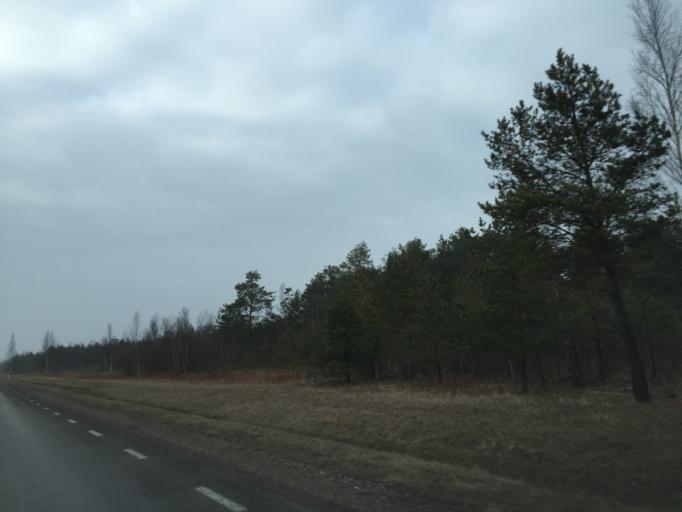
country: EE
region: Saare
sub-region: Orissaare vald
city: Orissaare
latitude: 58.5773
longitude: 23.3678
